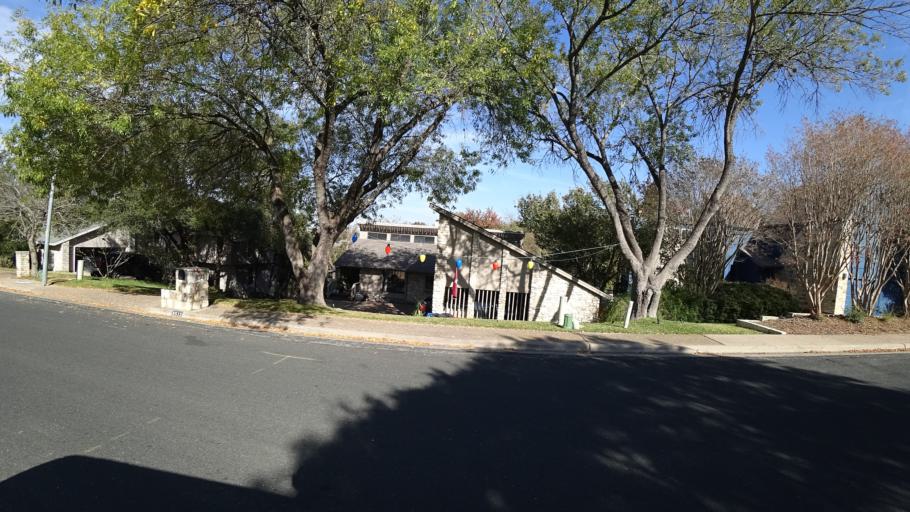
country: US
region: Texas
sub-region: Williamson County
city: Jollyville
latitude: 30.3825
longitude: -97.7616
